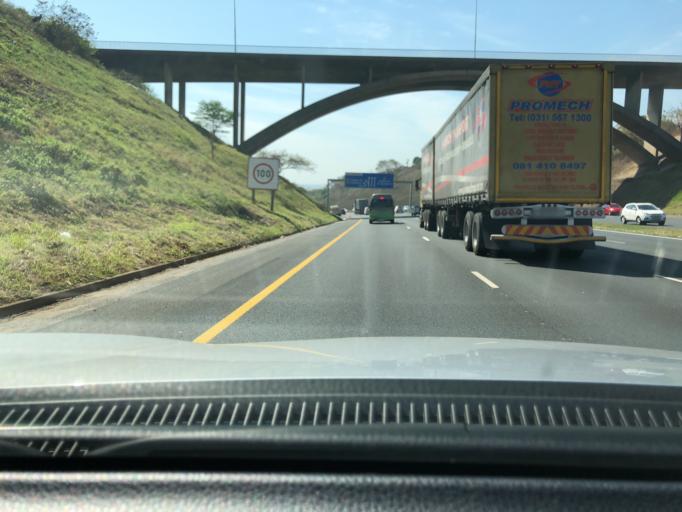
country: ZA
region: KwaZulu-Natal
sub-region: eThekwini Metropolitan Municipality
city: Berea
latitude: -29.8182
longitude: 30.9706
